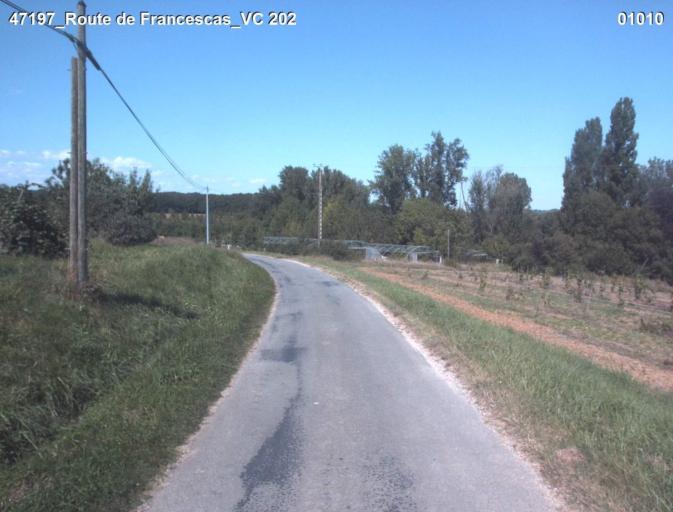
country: FR
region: Aquitaine
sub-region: Departement du Lot-et-Garonne
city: Laplume
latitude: 44.0705
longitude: 0.4648
